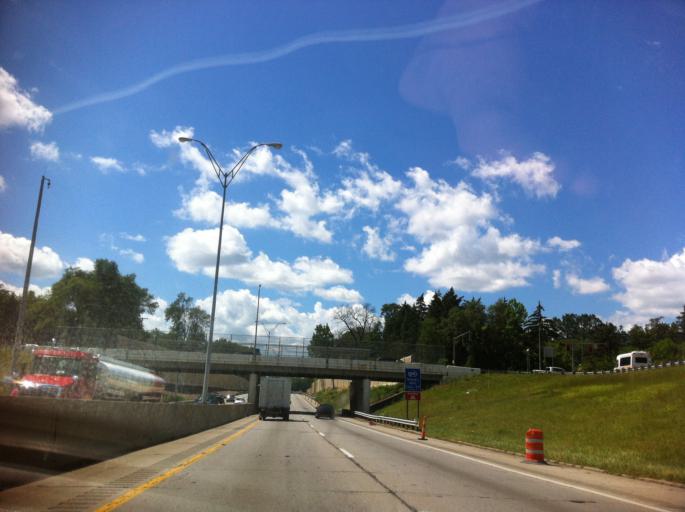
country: US
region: Ohio
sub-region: Lucas County
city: Ottawa Hills
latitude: 41.6881
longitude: -83.6434
